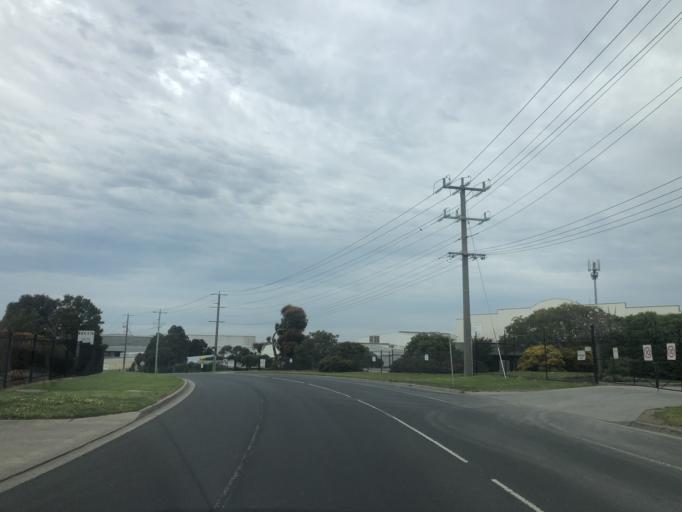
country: AU
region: Victoria
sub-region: Casey
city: Hallam
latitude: -38.0096
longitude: 145.2633
